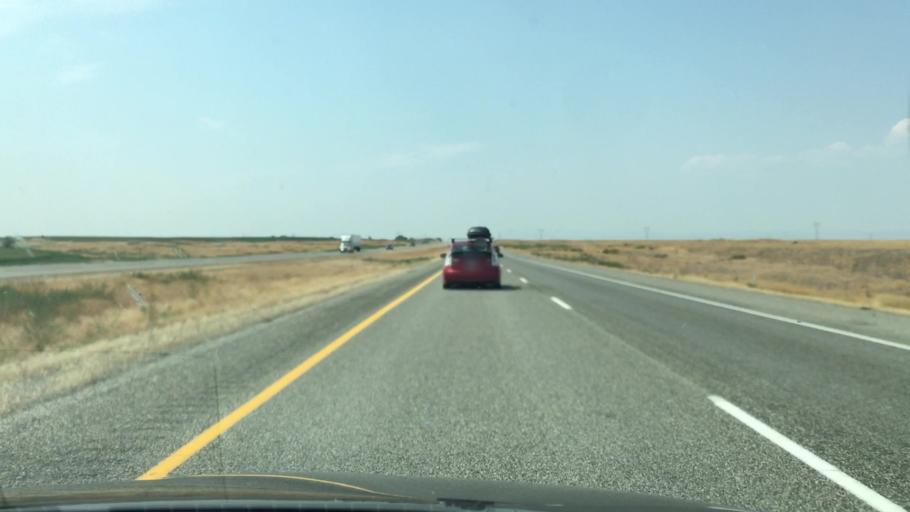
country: US
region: Idaho
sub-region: Gooding County
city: Wendell
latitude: 42.8242
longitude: -114.7950
